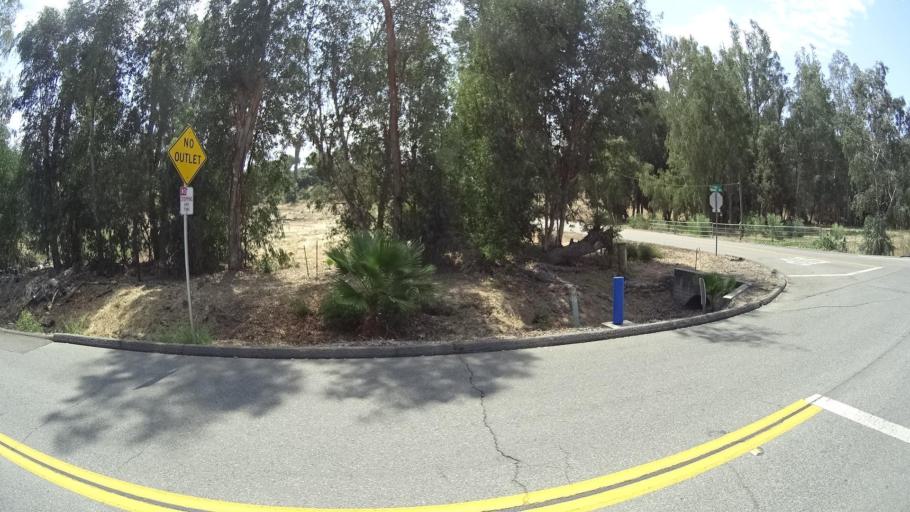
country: US
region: California
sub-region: San Diego County
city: Escondido
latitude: 33.1649
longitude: -117.0838
